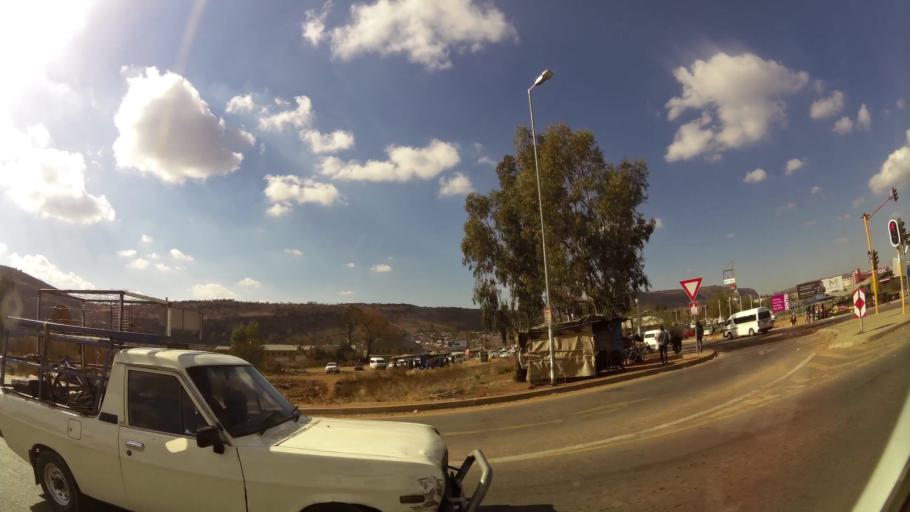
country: ZA
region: Gauteng
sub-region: City of Tshwane Metropolitan Municipality
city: Cullinan
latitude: -25.6980
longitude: 28.4199
